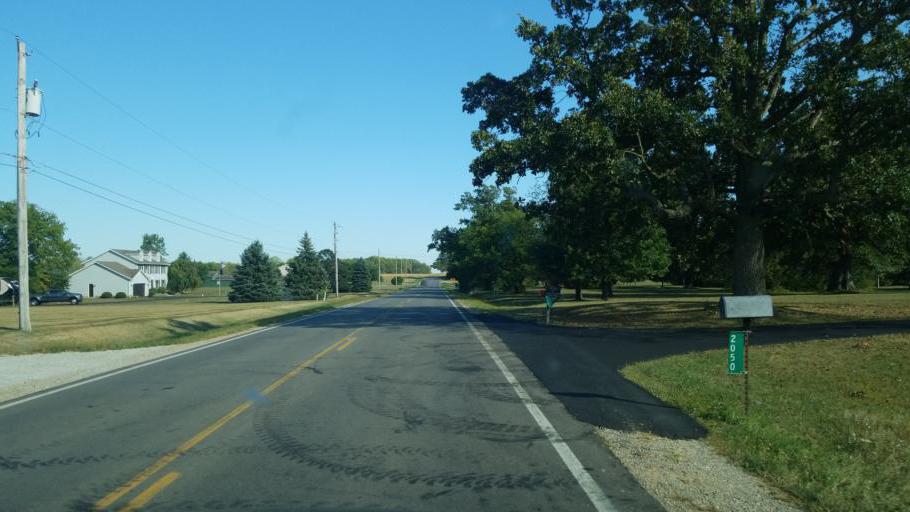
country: US
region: Ohio
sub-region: Madison County
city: Choctaw Lake
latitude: 39.9479
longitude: -83.4777
